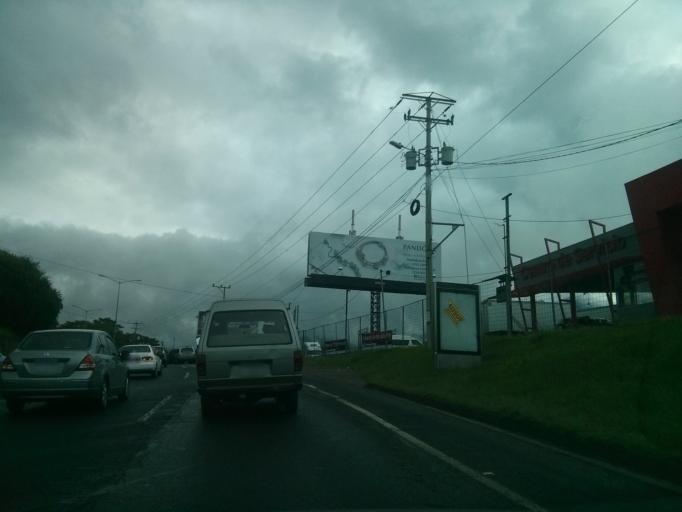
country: CR
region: San Jose
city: San Rafael
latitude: 9.9297
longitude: -84.1164
